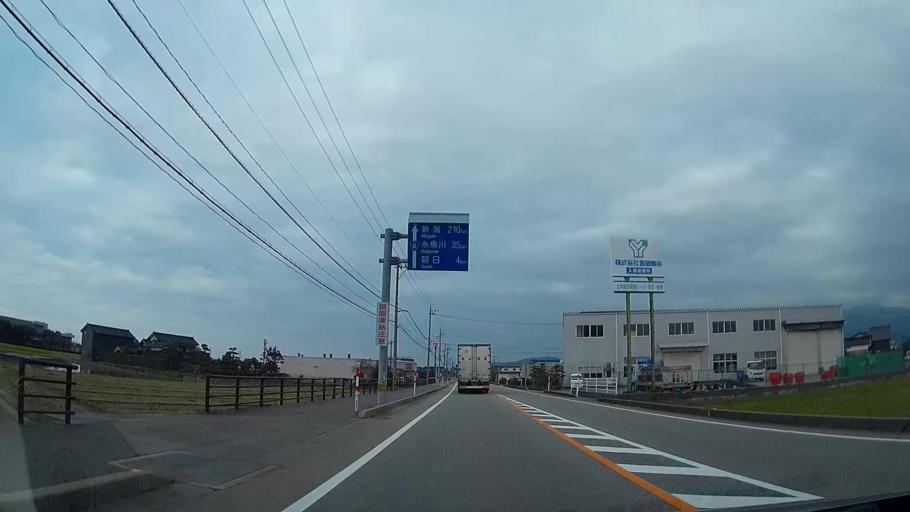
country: JP
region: Toyama
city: Nyuzen
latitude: 36.9412
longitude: 137.5177
